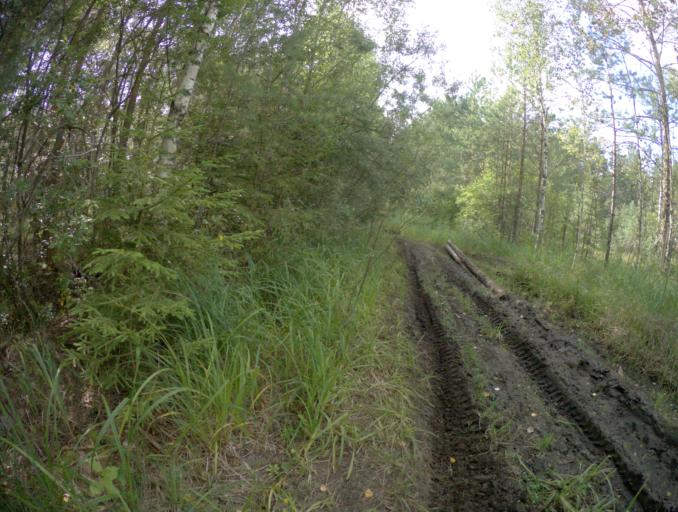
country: RU
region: Vladimir
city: Sobinka
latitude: 55.9202
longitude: 40.0738
